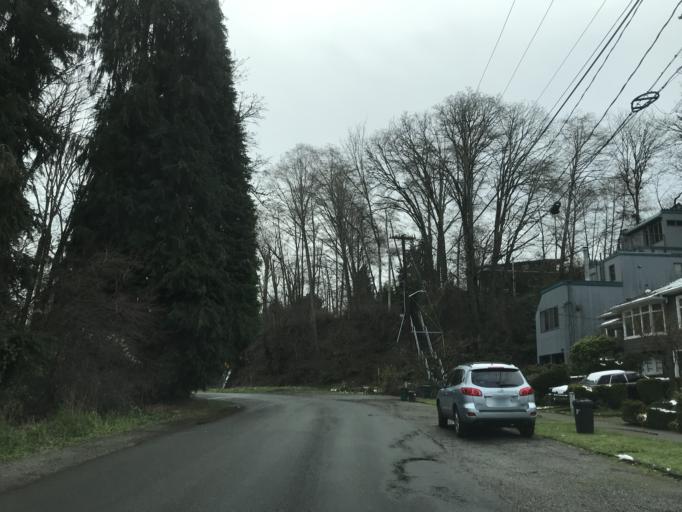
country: US
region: Washington
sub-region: King County
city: Seattle
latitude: 47.6300
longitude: -122.2991
